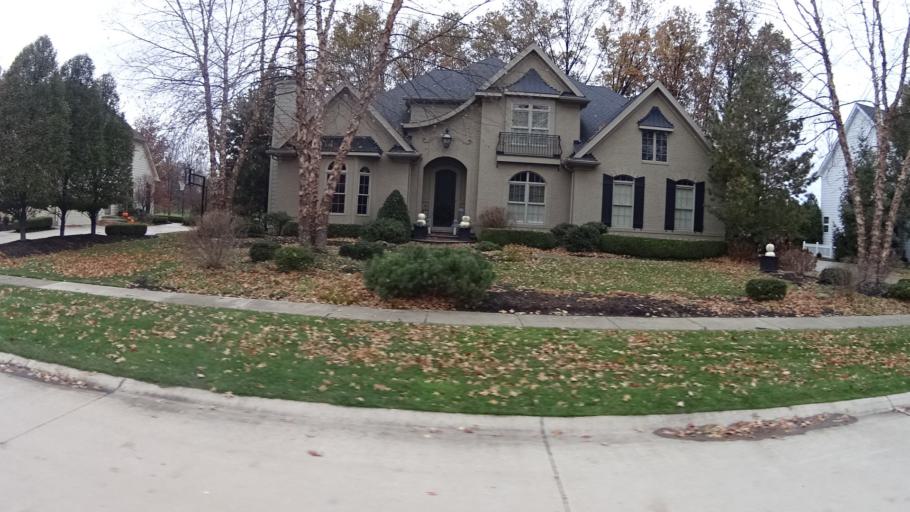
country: US
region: Ohio
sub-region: Lorain County
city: Avon Lake
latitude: 41.4886
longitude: -82.0044
